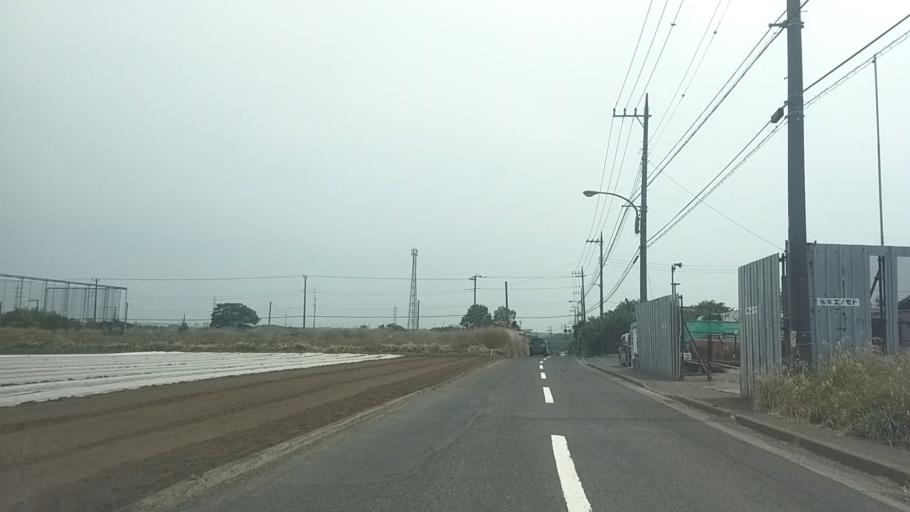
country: JP
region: Kanagawa
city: Fujisawa
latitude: 35.3971
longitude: 139.4342
